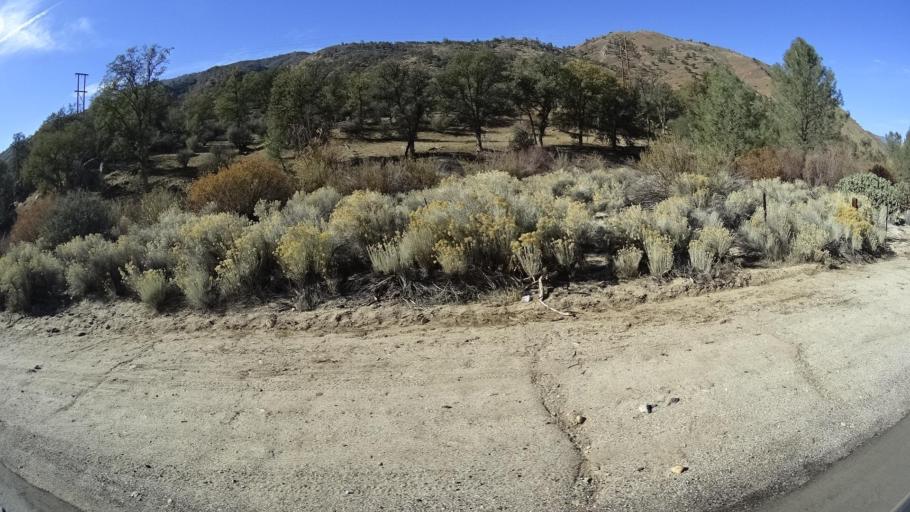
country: US
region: California
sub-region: Kern County
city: Bodfish
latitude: 35.5250
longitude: -118.5119
